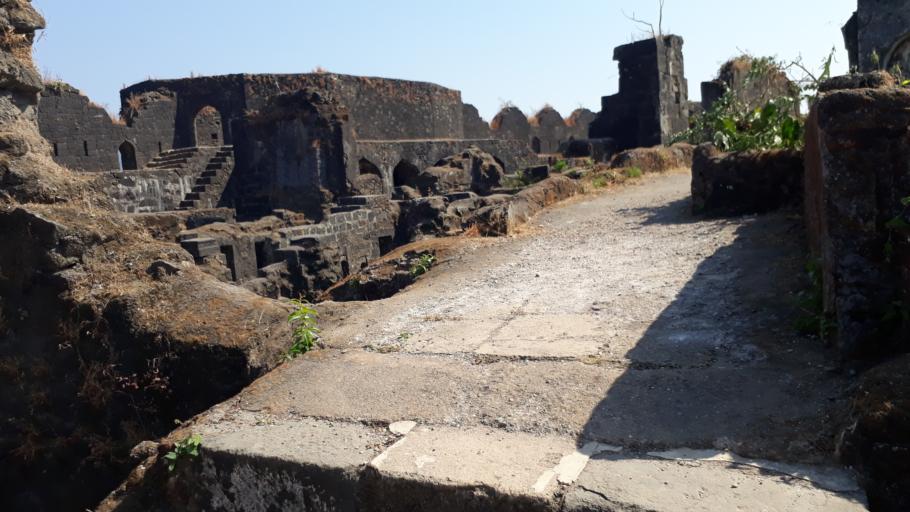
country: IN
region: Maharashtra
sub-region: Raigarh
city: Murud
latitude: 18.3008
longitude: 72.9649
